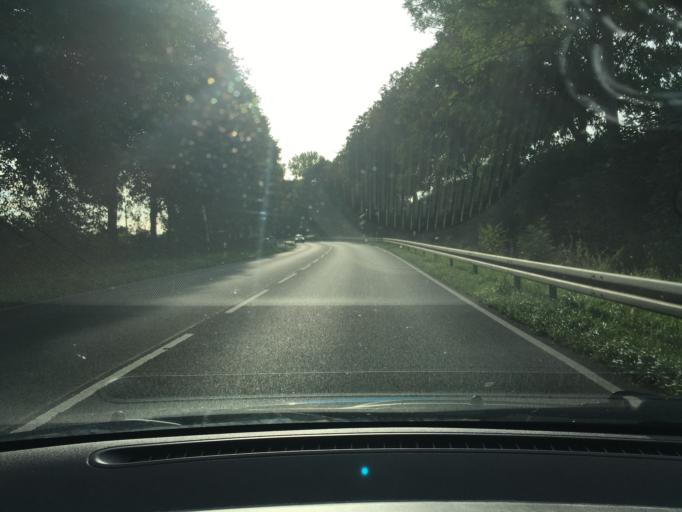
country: DE
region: Lower Saxony
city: Bad Munder am Deister
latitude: 52.1723
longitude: 9.5113
